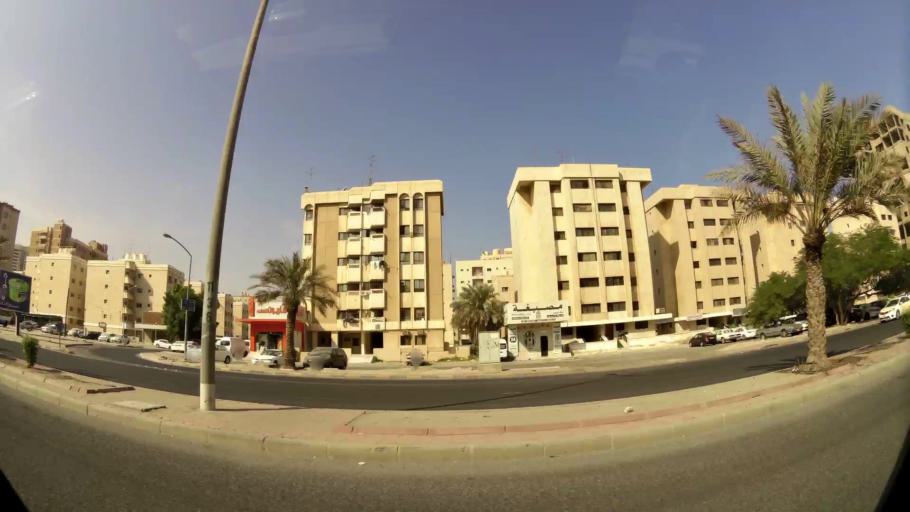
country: KW
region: Al Ahmadi
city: Al Mahbulah
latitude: 29.1374
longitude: 48.1263
